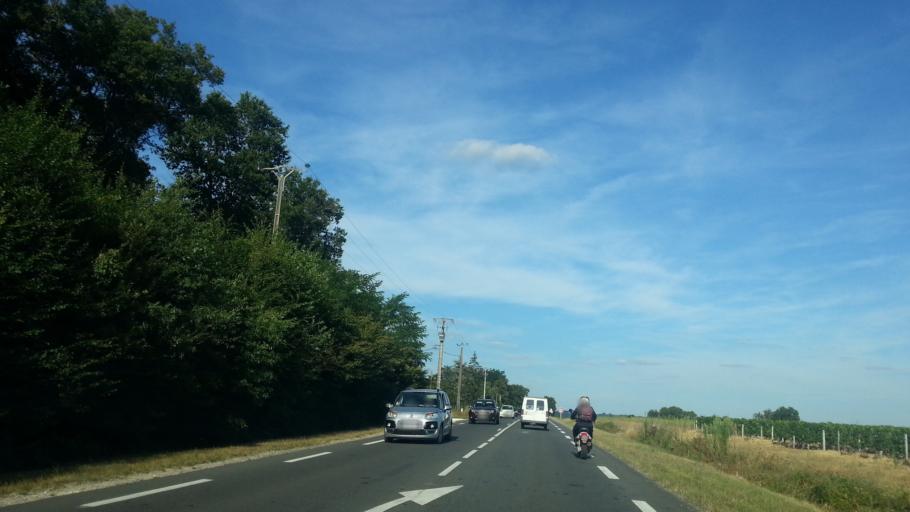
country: FR
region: Aquitaine
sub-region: Departement de la Gironde
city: Ayguemorte-les-Graves
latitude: 44.6978
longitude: -0.4733
